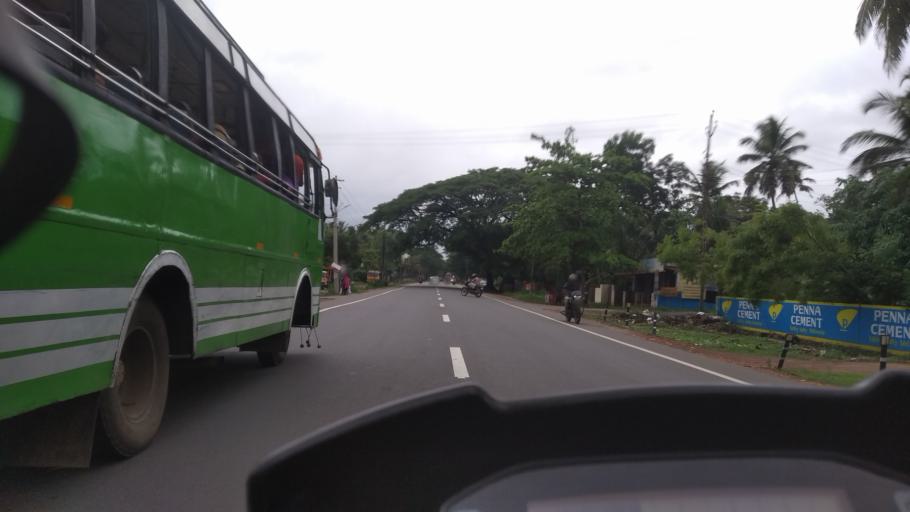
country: IN
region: Kerala
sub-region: Alappuzha
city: Alleppey
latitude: 9.4549
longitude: 76.3410
